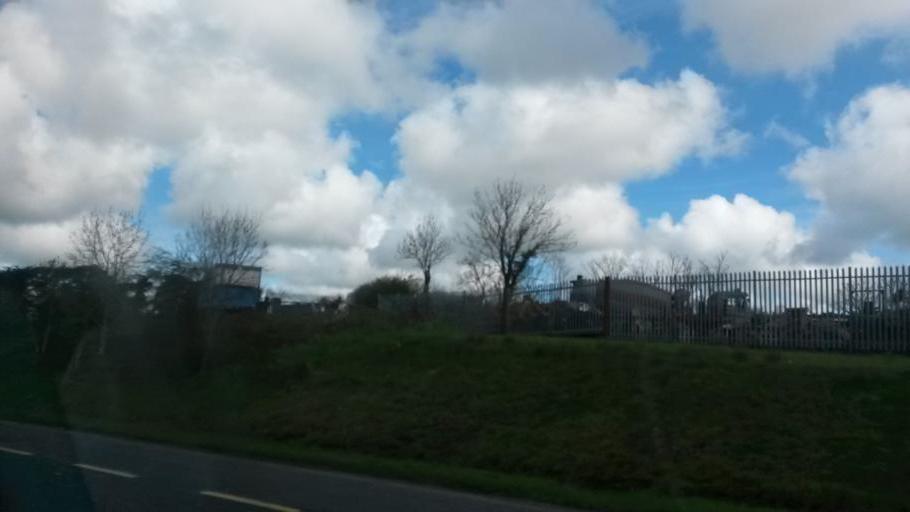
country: IE
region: Ulster
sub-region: An Cabhan
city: Ballyjamesduff
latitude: 53.9055
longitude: -7.1878
